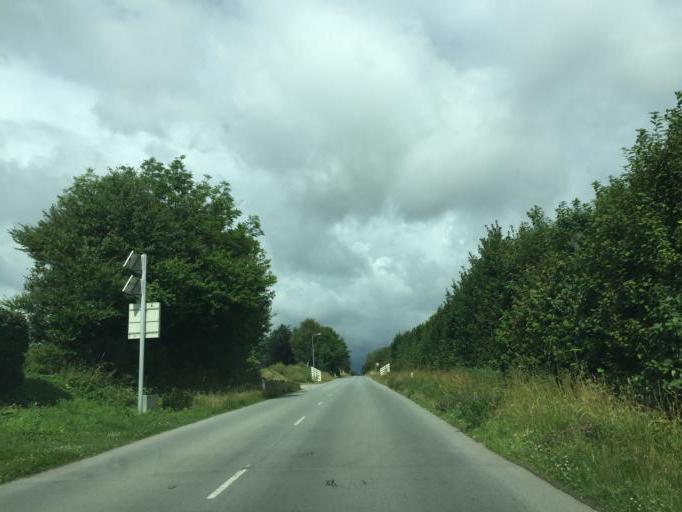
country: DK
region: South Denmark
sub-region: Faaborg-Midtfyn Kommune
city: Arslev
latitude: 55.2833
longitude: 10.4845
